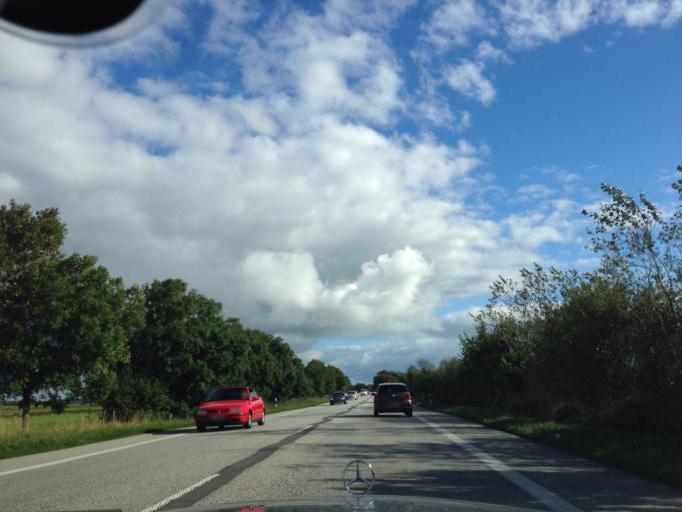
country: DE
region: Schleswig-Holstein
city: Risum-Lindholm
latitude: 54.7554
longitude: 8.8912
